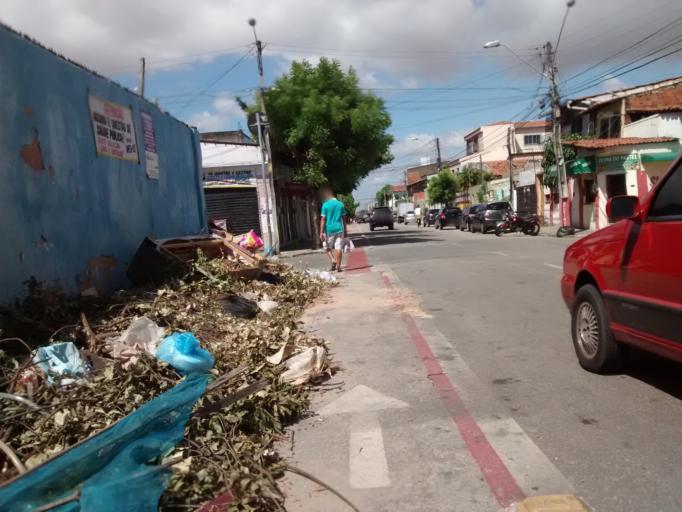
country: BR
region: Ceara
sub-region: Fortaleza
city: Fortaleza
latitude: -3.7258
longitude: -38.5514
